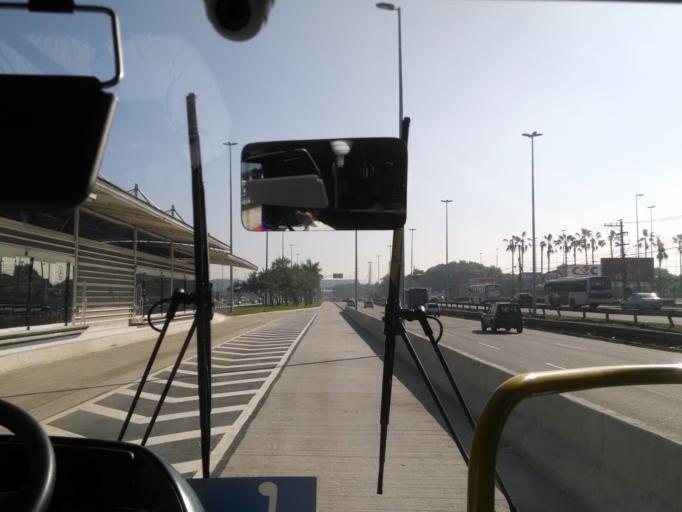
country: BR
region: Rio de Janeiro
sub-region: Rio De Janeiro
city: Rio de Janeiro
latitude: -22.9841
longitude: -43.3656
